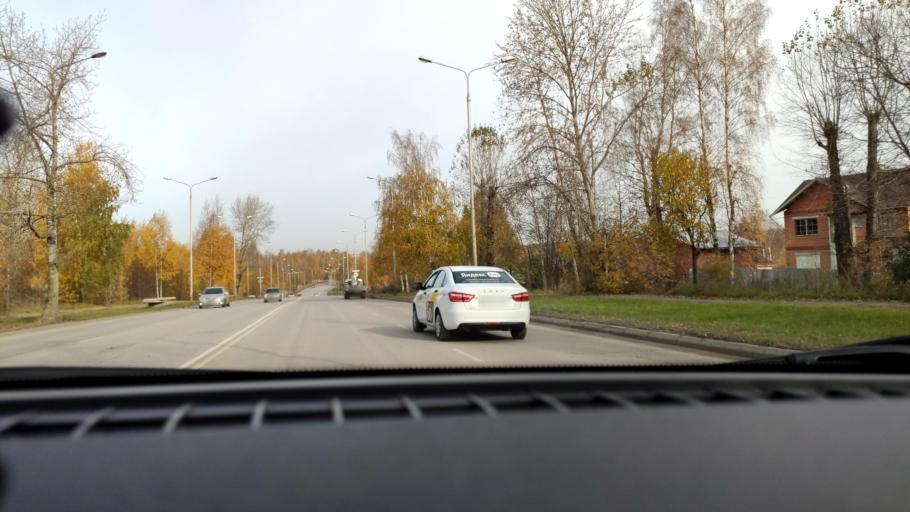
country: RU
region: Perm
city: Perm
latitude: 58.0936
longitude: 56.3837
